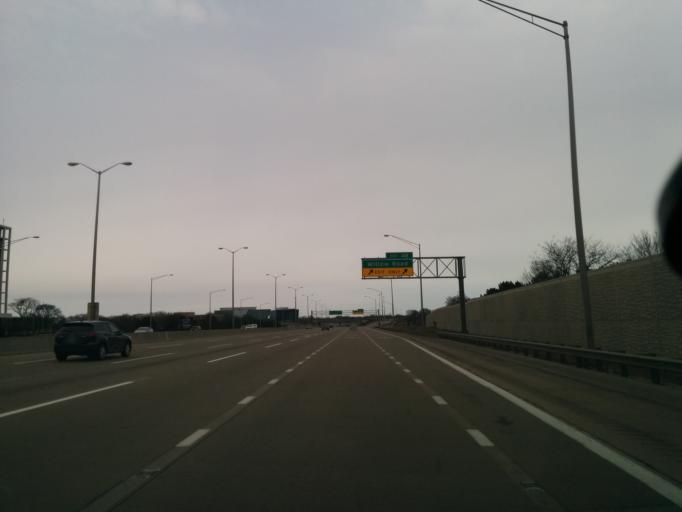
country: US
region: Illinois
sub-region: Cook County
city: Northbrook
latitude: 42.0991
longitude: -87.8679
